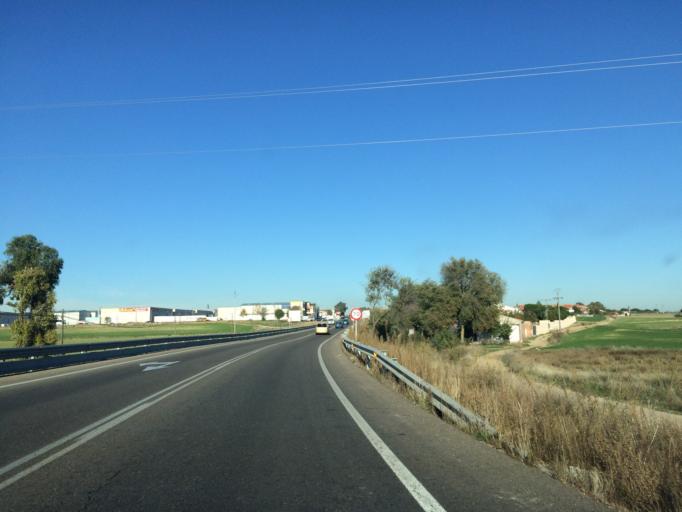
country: ES
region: Castille-La Mancha
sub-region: Province of Toledo
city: Carranque
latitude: 40.1785
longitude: -3.8896
